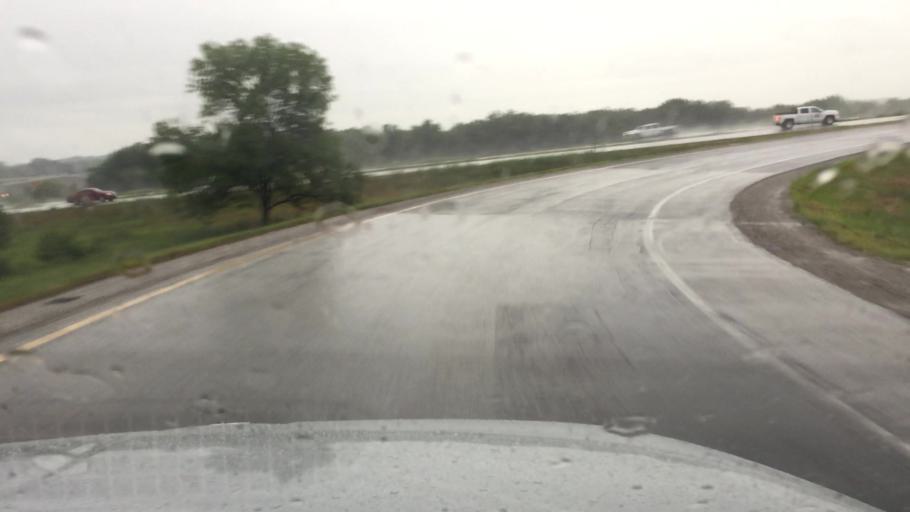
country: US
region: Iowa
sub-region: Johnson County
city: Tiffin
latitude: 41.6959
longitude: -91.6405
